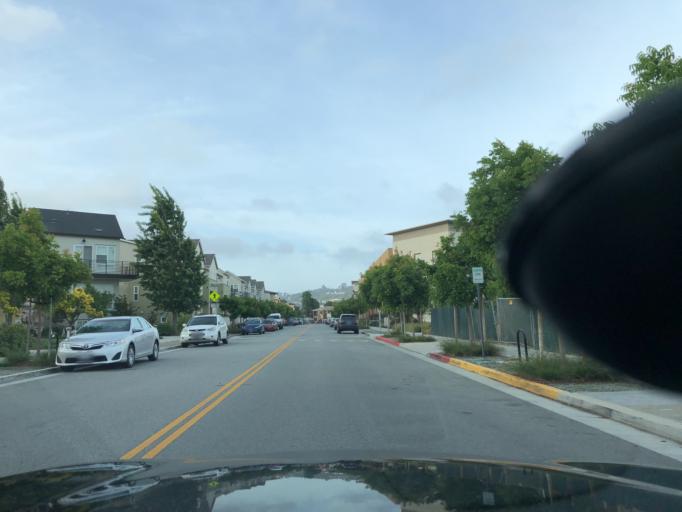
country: US
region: California
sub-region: San Mateo County
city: Foster City
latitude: 37.5424
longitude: -122.2967
